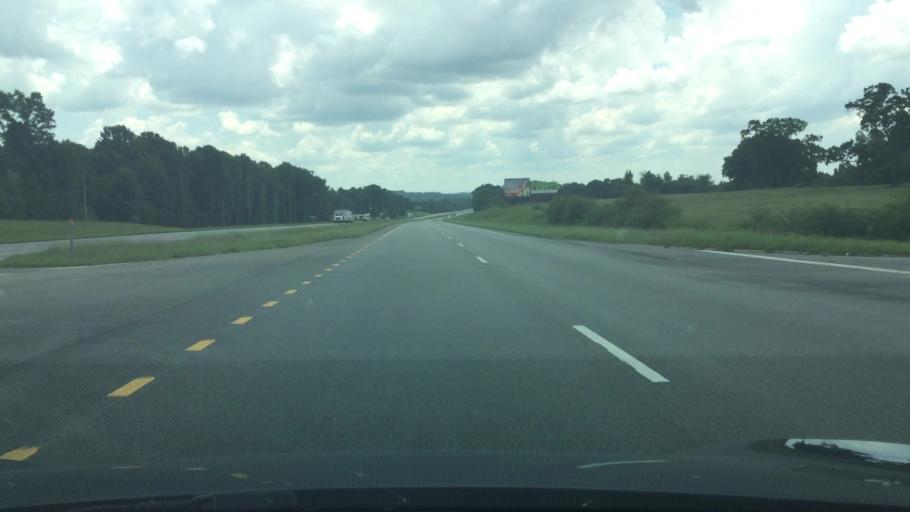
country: US
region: Alabama
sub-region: Pike County
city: Troy
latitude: 31.8756
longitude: -86.0030
